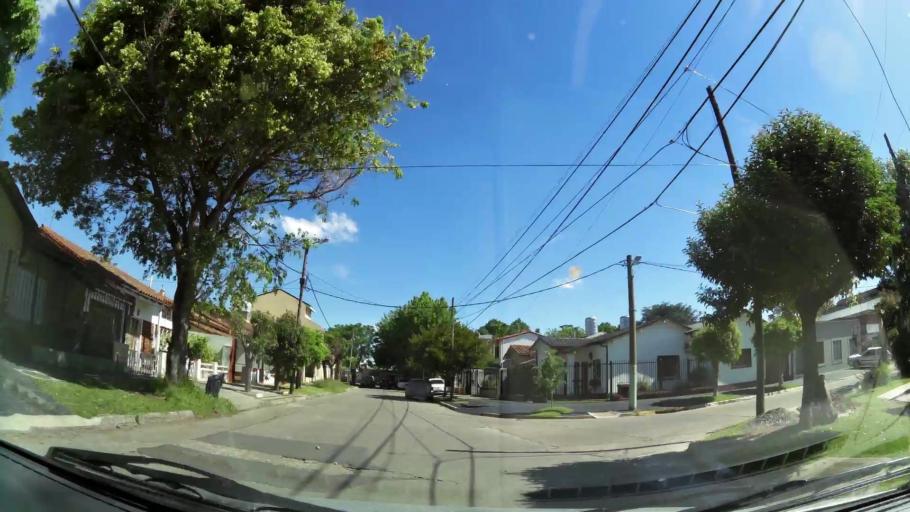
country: AR
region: Buenos Aires
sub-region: Partido de Lomas de Zamora
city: Lomas de Zamora
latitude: -34.7374
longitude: -58.4107
